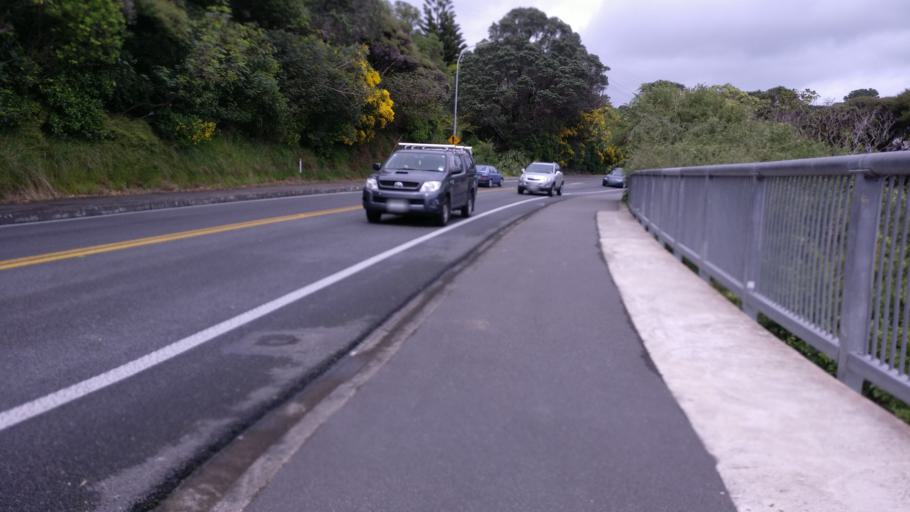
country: NZ
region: Wellington
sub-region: Porirua City
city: Porirua
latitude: -41.0337
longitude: 174.8888
